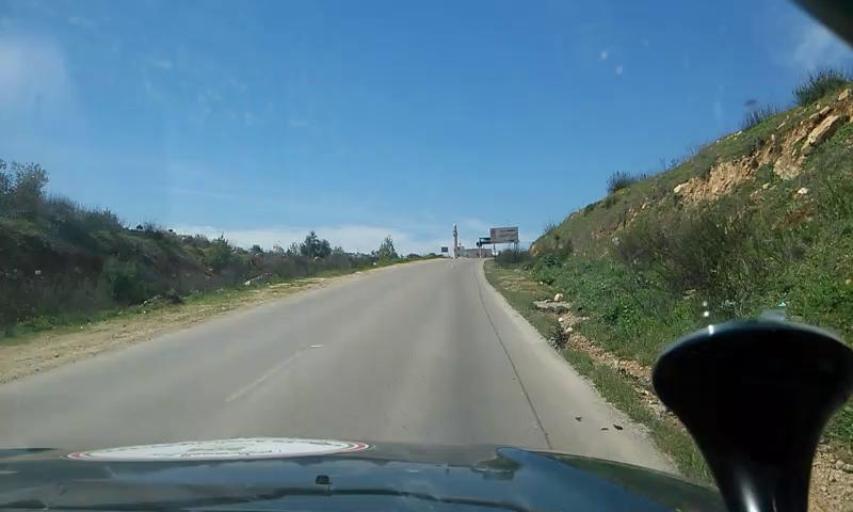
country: PS
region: West Bank
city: Biddu
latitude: 31.8387
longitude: 35.1579
